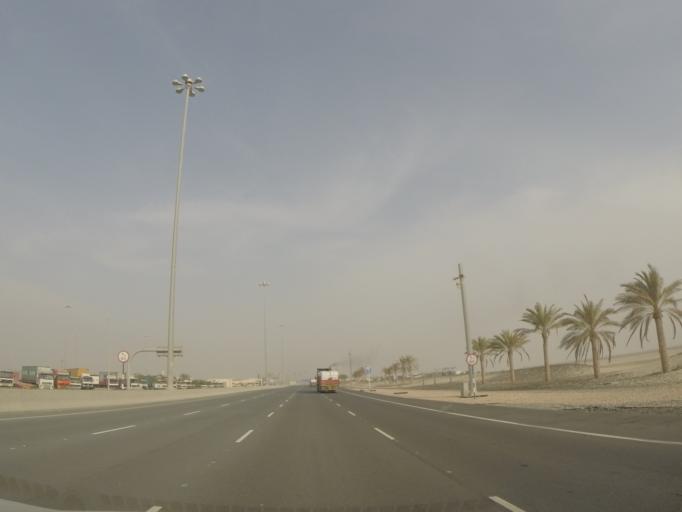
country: AE
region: Abu Dhabi
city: Abu Dhabi
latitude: 24.7795
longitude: 54.7066
